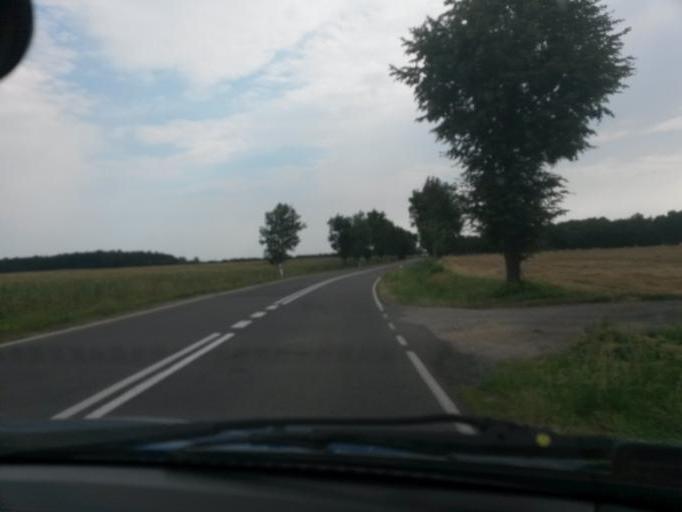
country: PL
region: Masovian Voivodeship
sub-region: Powiat zurominski
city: Lubowidz
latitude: 53.0905
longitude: 19.8666
